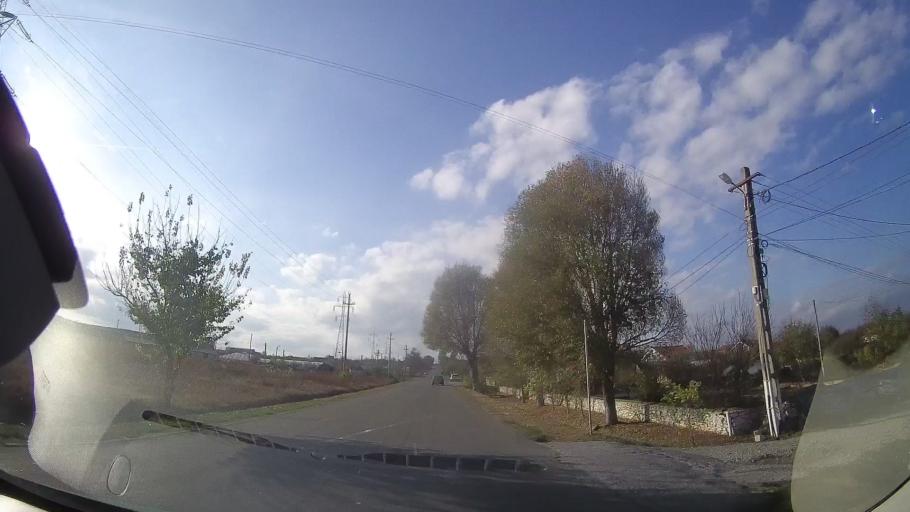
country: RO
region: Constanta
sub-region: Comuna Limanu
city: Limanu
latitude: 43.7940
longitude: 28.5353
